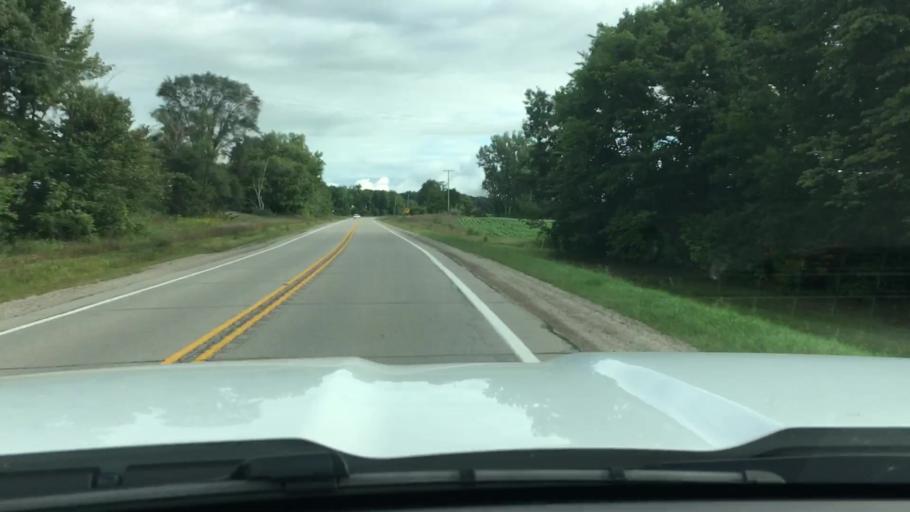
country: US
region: Michigan
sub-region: Tuscola County
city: Caro
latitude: 43.5291
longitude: -83.3456
